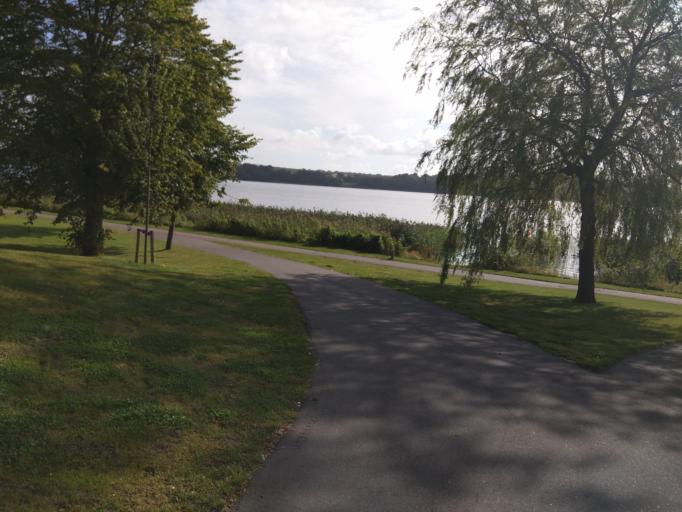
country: DK
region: Central Jutland
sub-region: Viborg Kommune
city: Viborg
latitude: 56.4421
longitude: 9.4048
